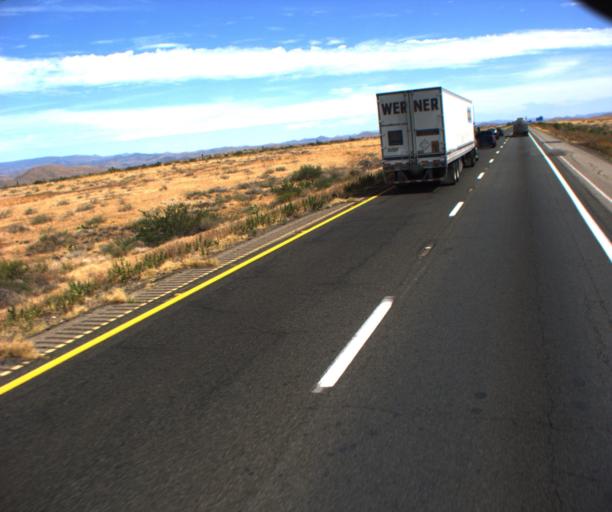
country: US
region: Arizona
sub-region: Yavapai County
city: Black Canyon City
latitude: 34.1721
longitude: -112.1359
